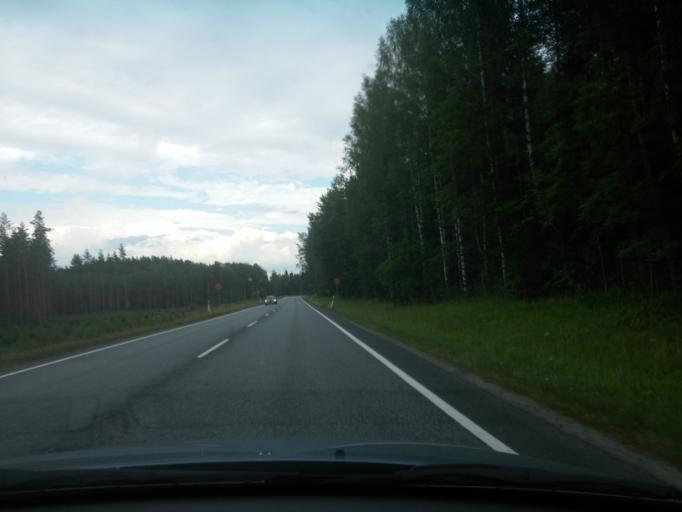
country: FI
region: Haeme
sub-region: Haemeenlinna
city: Tervakoski
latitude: 60.7425
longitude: 24.6382
